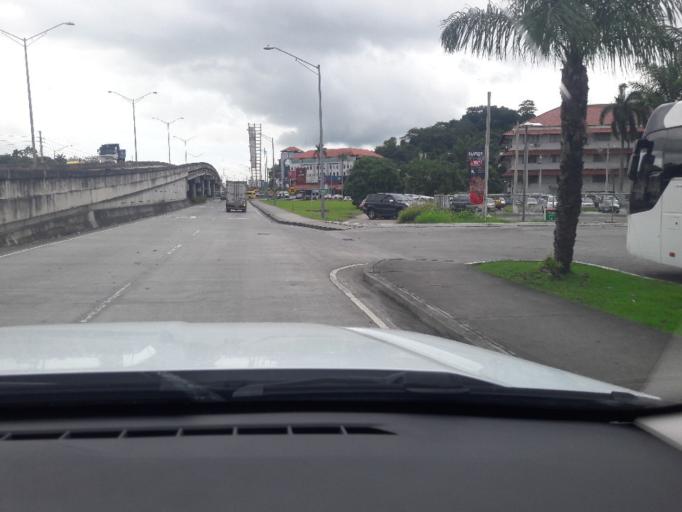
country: PA
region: Panama
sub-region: Distrito de Panama
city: Ancon
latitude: 8.9703
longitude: -79.5629
